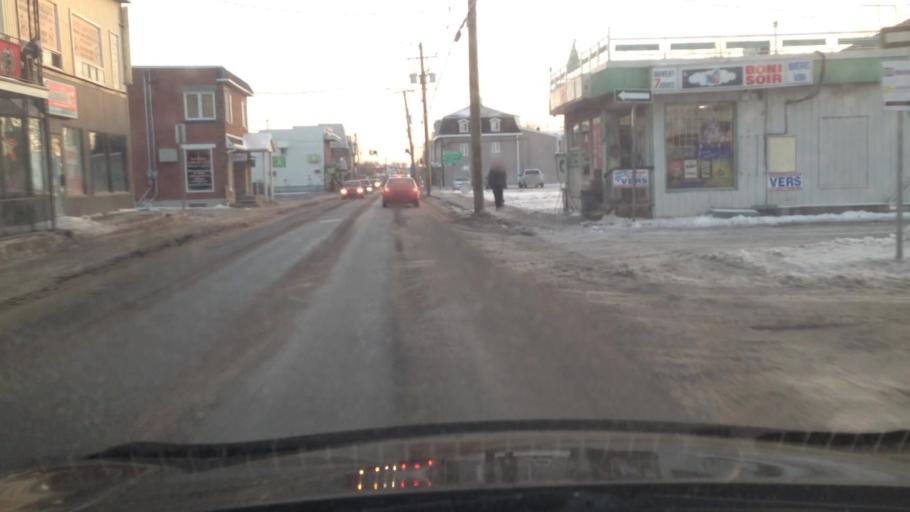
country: CA
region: Quebec
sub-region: Lanaudiere
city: Saint-Lin-Laurentides
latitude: 45.8542
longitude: -73.7572
